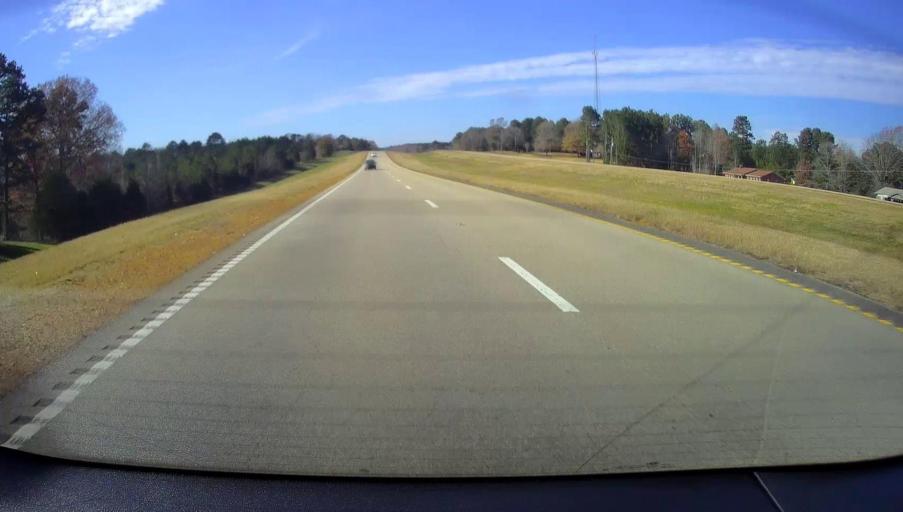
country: US
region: Mississippi
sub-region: Benton County
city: Ashland
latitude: 34.9532
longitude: -89.0117
